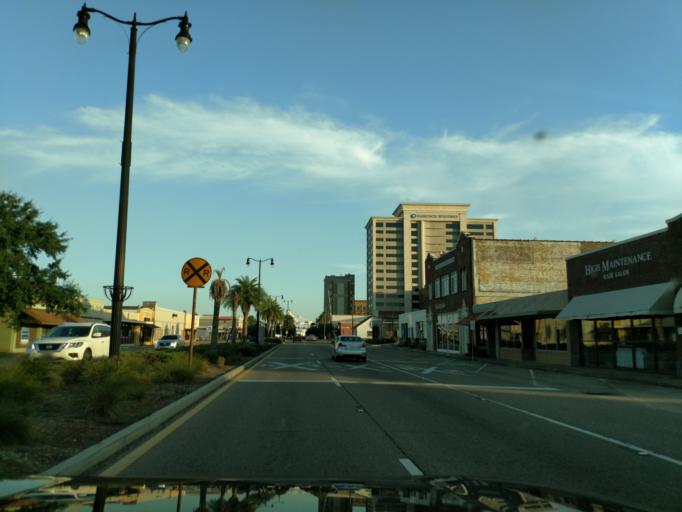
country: US
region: Mississippi
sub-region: Harrison County
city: Gulfport
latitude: 30.3709
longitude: -89.0930
